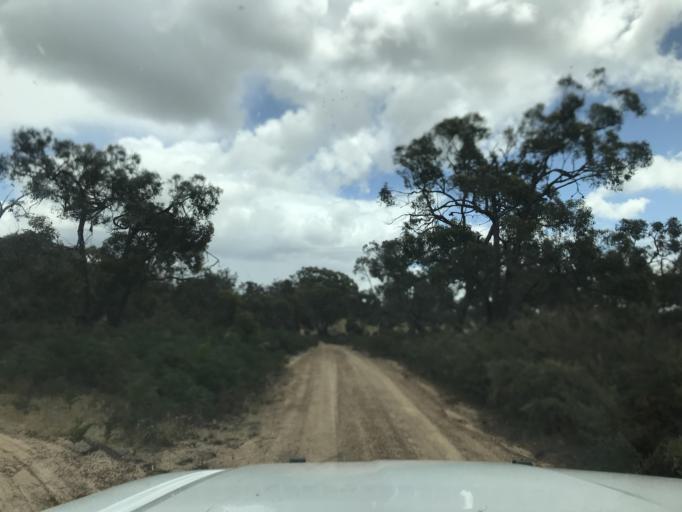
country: AU
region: South Australia
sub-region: Wattle Range
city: Penola
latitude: -37.0889
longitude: 141.3345
